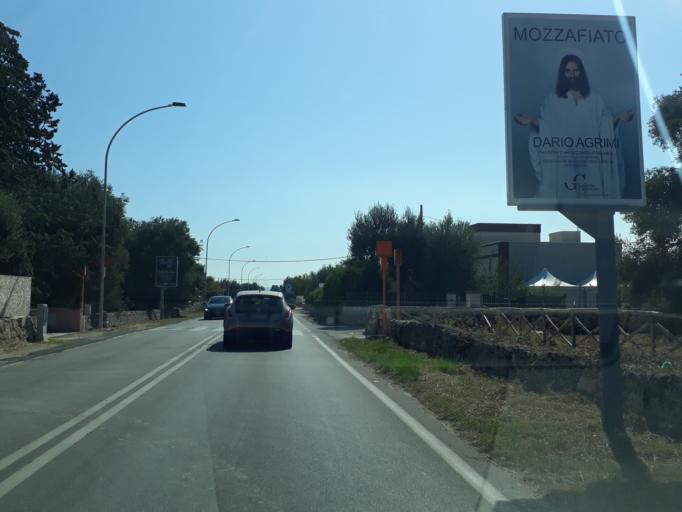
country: IT
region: Apulia
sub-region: Provincia di Bari
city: Monopoli
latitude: 40.9376
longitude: 17.3083
